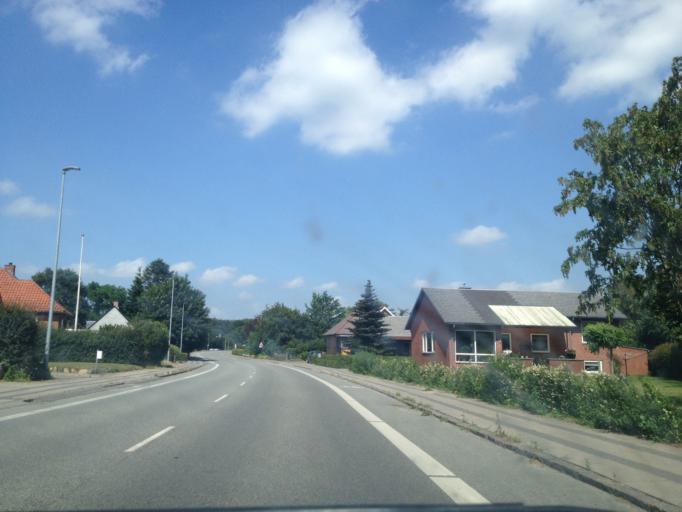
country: DK
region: South Denmark
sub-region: Kolding Kommune
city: Vamdrup
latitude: 55.4304
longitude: 9.2884
